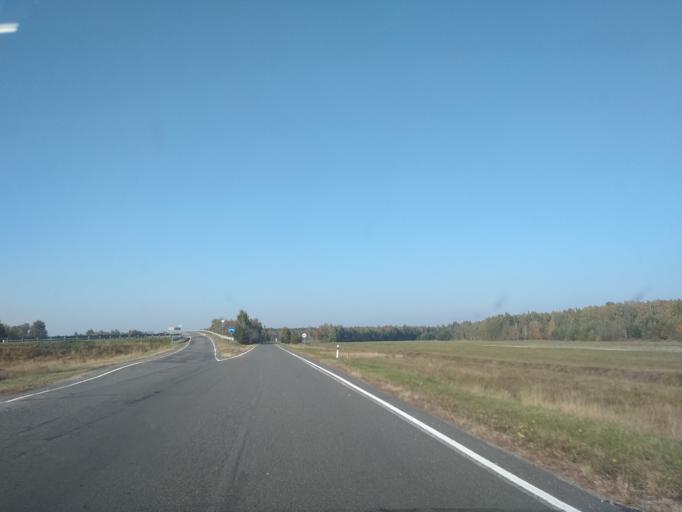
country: BY
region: Brest
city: Horad Kobryn
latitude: 52.2211
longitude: 24.4257
